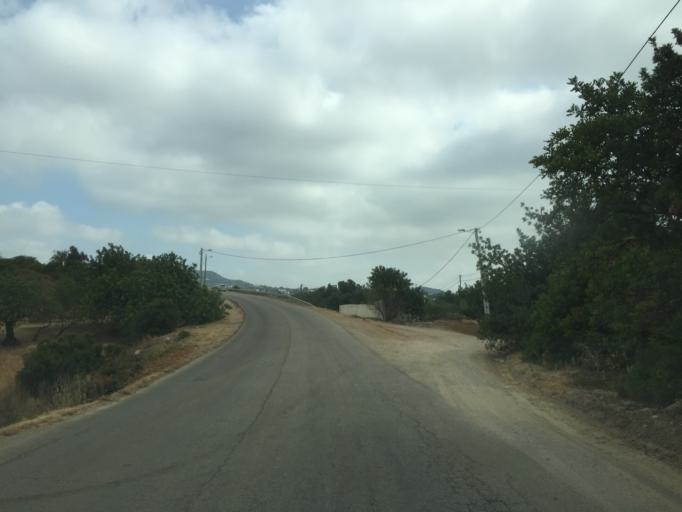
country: PT
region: Faro
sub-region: Faro
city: Santa Barbara de Nexe
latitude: 37.0925
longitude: -7.9778
